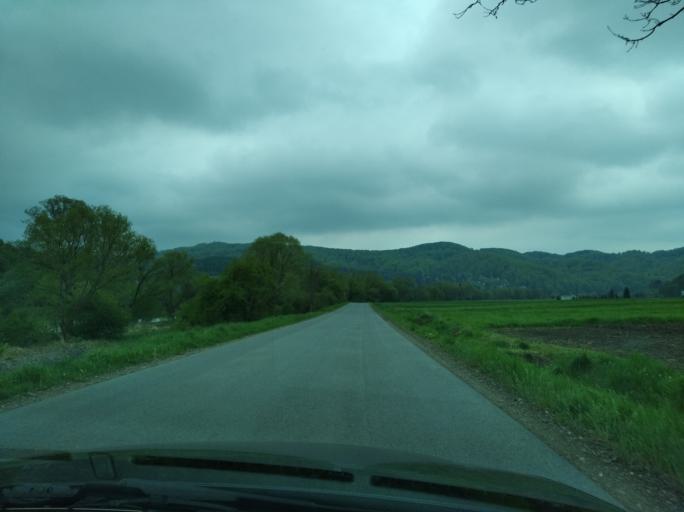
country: PL
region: Subcarpathian Voivodeship
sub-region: Powiat sanocki
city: Sanok
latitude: 49.6028
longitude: 22.2341
